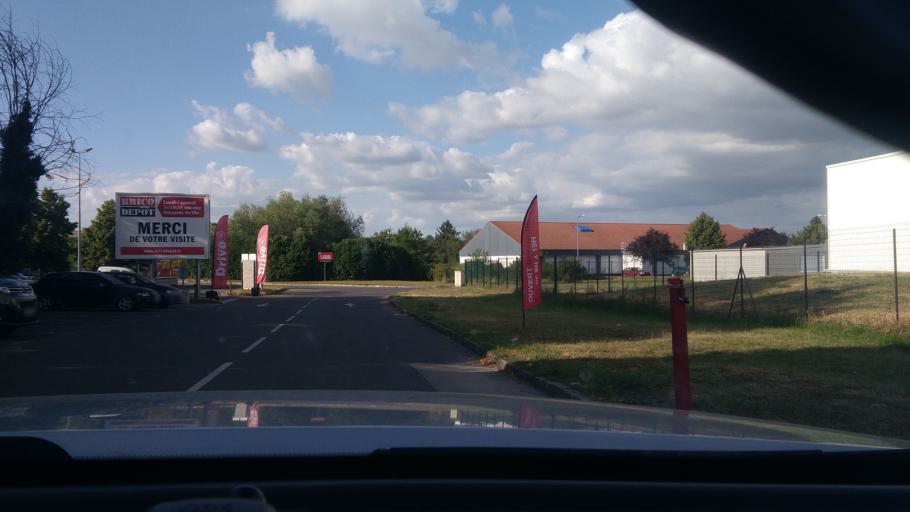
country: FR
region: Ile-de-France
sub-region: Departement de Seine-et-Marne
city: Cannes-Ecluse
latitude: 48.3589
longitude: 2.9830
